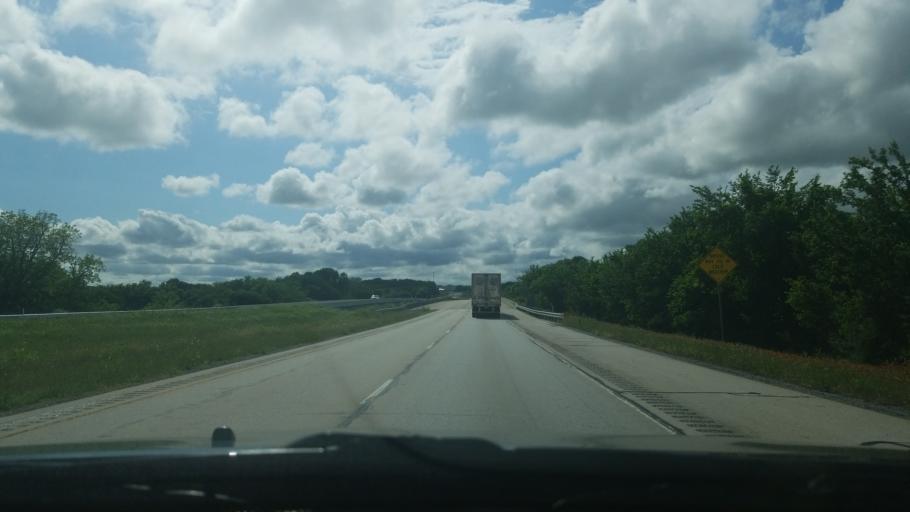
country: US
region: Texas
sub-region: Denton County
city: Ponder
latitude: 33.2488
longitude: -97.4016
